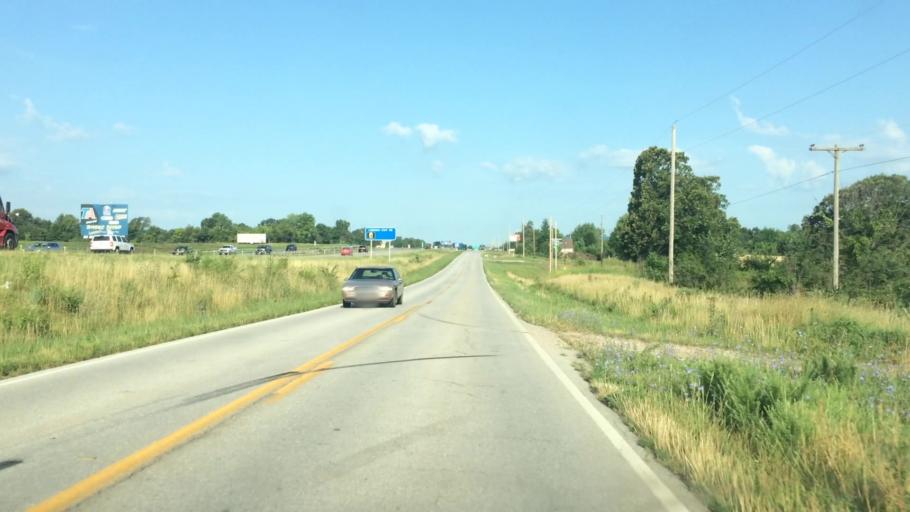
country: US
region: Missouri
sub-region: Greene County
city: Strafford
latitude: 37.2710
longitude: -93.0843
